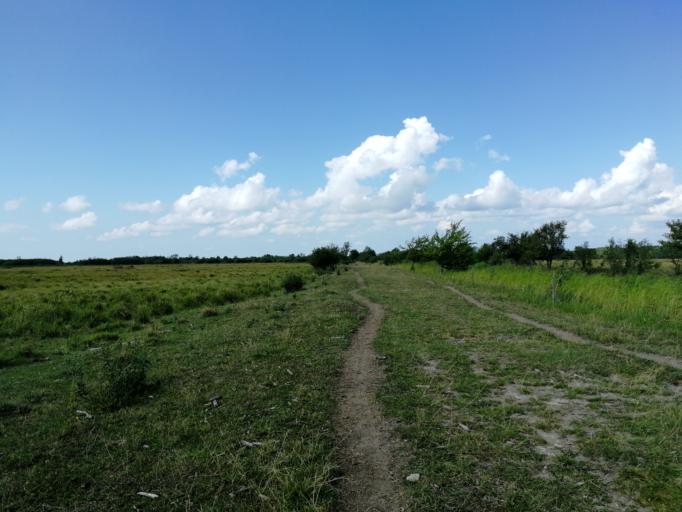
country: EE
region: Laeaene
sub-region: Lihula vald
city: Lihula
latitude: 58.7211
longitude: 23.8086
